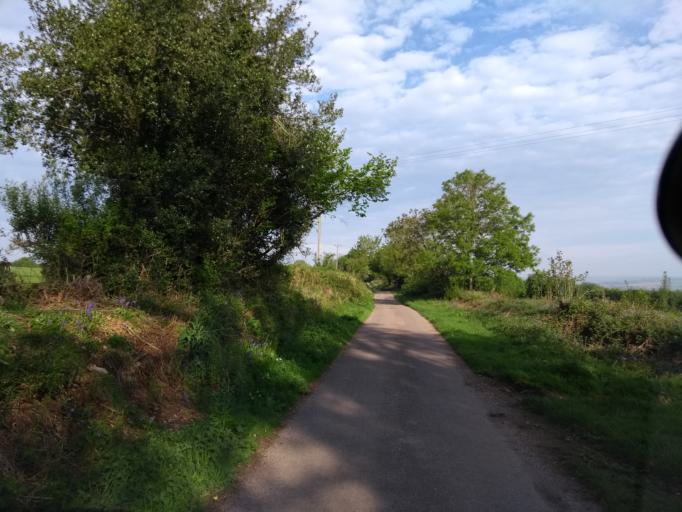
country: GB
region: England
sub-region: Dorset
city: Lyme Regis
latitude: 50.7982
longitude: -2.9264
